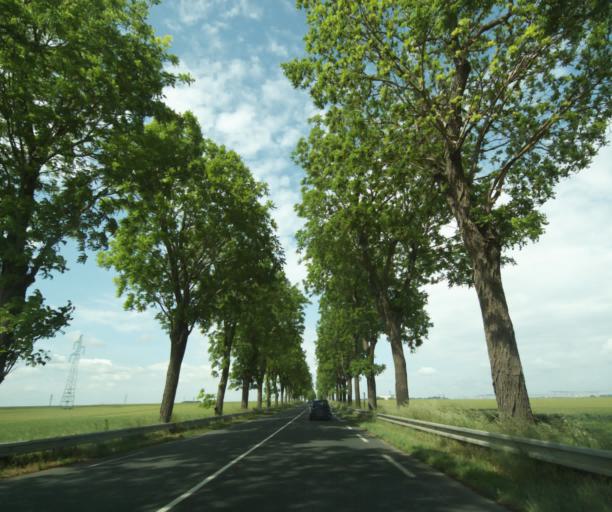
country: FR
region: Pays de la Loire
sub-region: Departement de Maine-et-Loire
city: Distre
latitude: 47.2015
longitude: -0.1224
